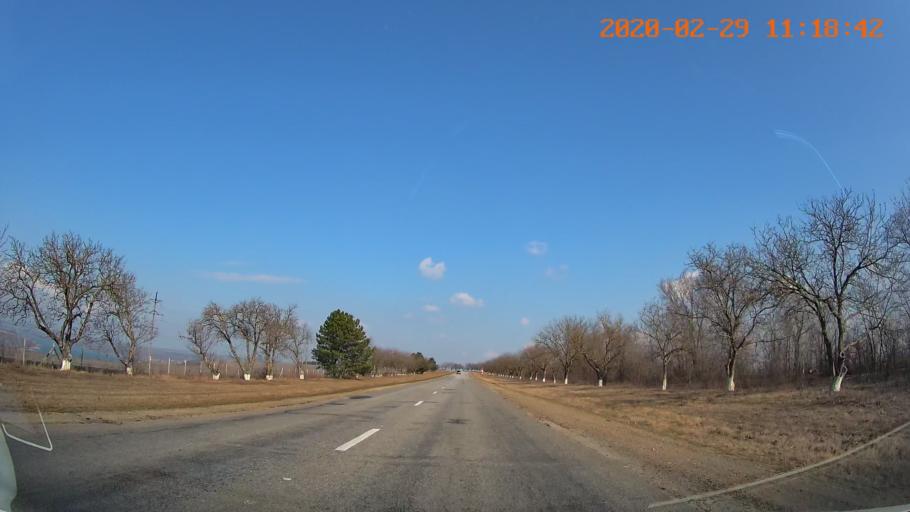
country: MD
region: Telenesti
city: Cocieri
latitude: 47.3388
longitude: 29.1747
